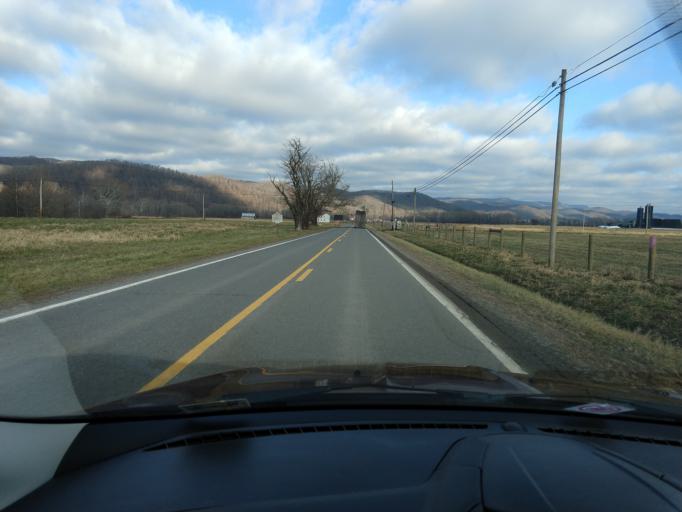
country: US
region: West Virginia
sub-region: Randolph County
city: Elkins
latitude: 38.6957
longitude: -79.9748
